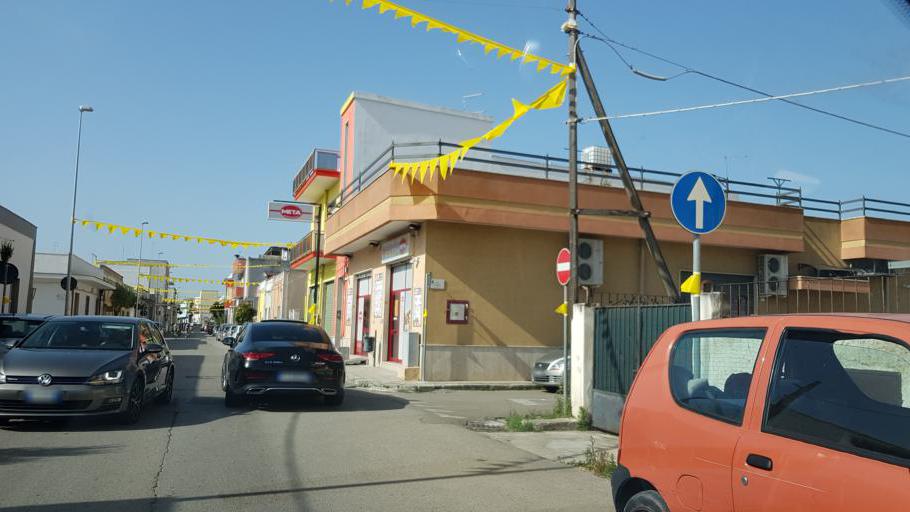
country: IT
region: Apulia
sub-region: Provincia di Brindisi
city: San Pancrazio Salentino
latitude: 40.4226
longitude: 17.8409
